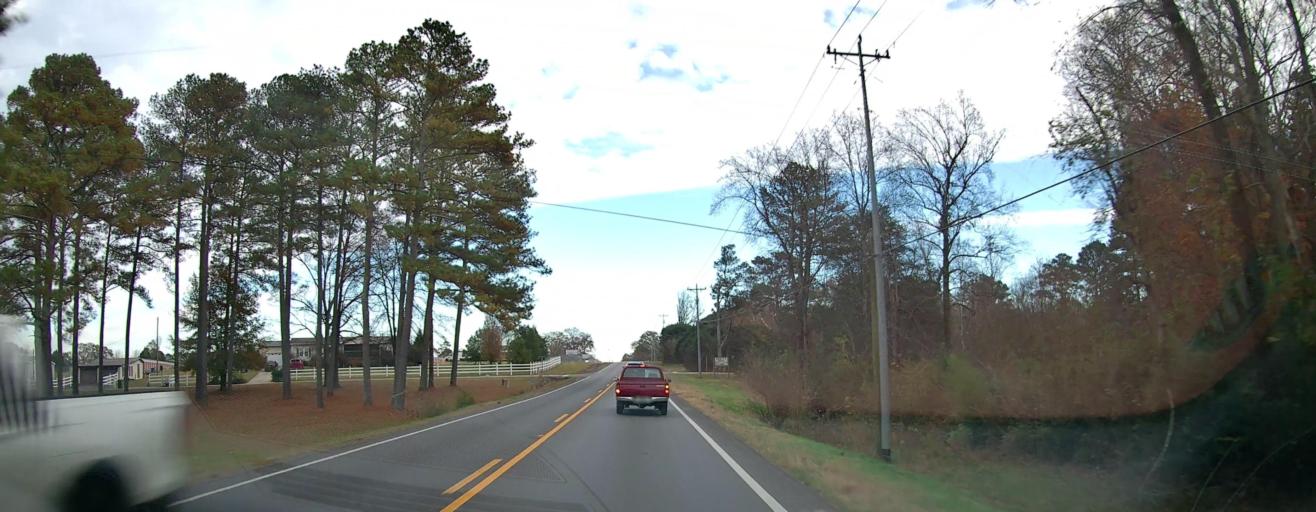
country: US
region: Alabama
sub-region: Morgan County
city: Priceville
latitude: 34.4749
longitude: -86.8092
